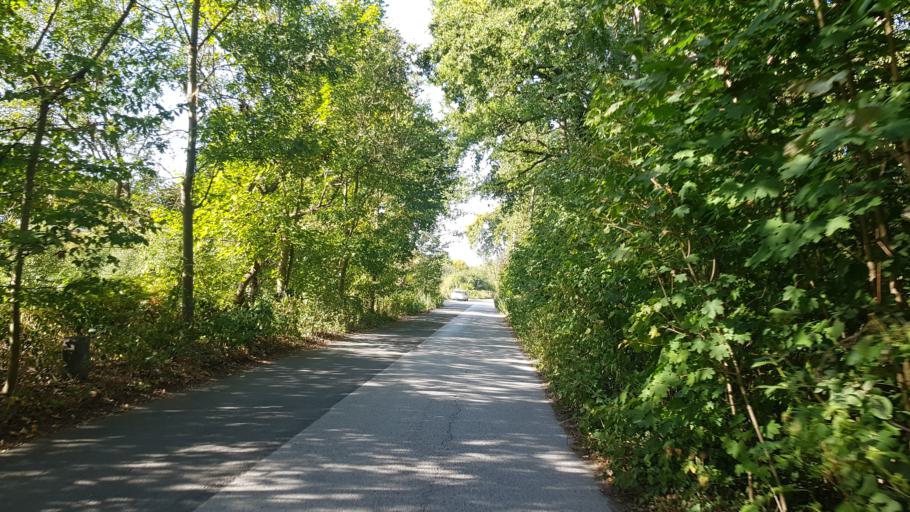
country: DE
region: North Rhine-Westphalia
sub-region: Regierungsbezirk Dusseldorf
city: Ratingen
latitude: 51.3550
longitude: 6.8198
